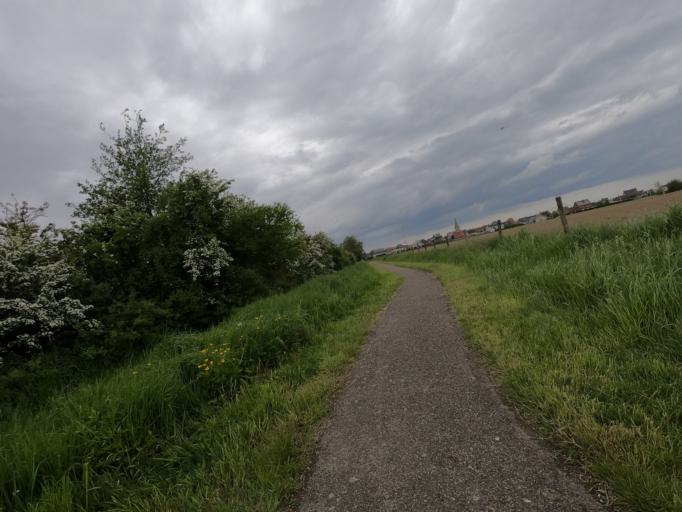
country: BE
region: Flanders
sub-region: Provincie West-Vlaanderen
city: Poperinge
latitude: 50.9288
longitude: 2.7459
